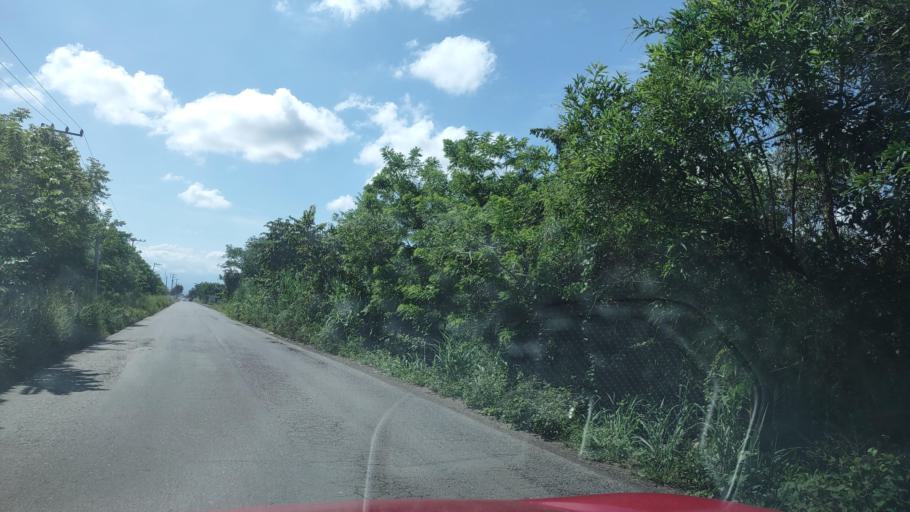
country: MX
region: Veracruz
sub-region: Martinez de la Torre
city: La Union Paso Largo
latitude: 20.1354
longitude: -96.9976
